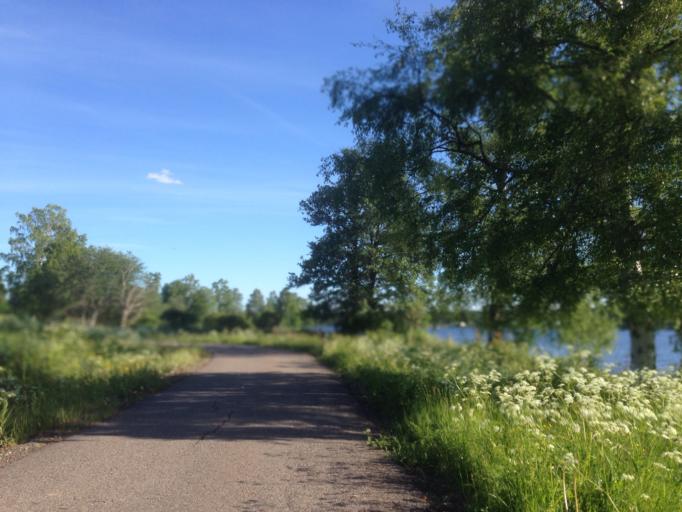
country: SE
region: Dalarna
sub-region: Ludvika Kommun
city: Ludvika
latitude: 60.1079
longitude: 15.2106
